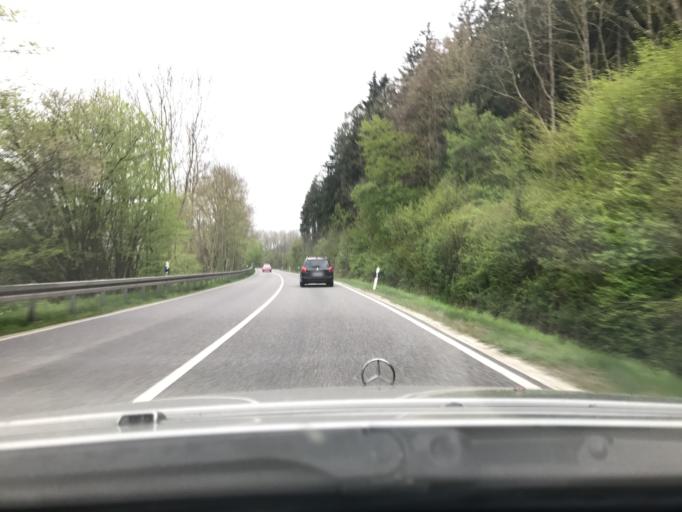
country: DE
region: Thuringia
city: Heilbad Heiligenstadt
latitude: 51.3636
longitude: 10.1684
